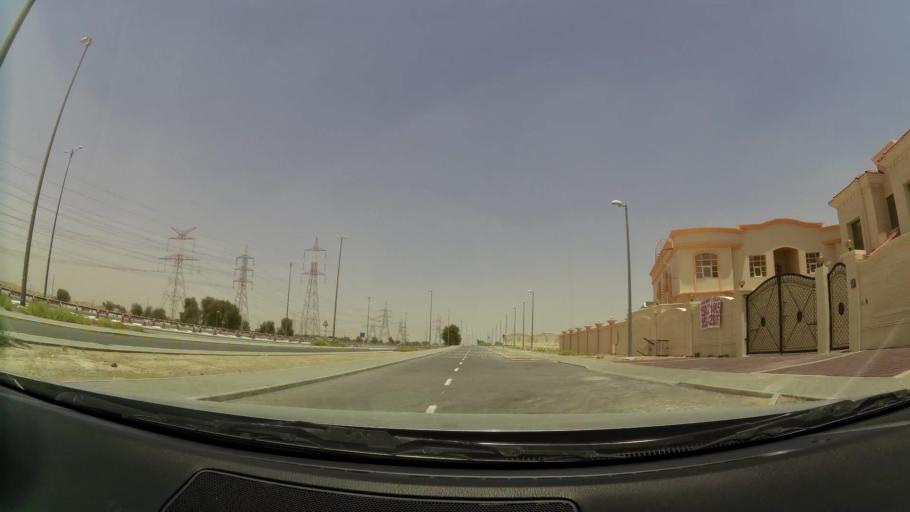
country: OM
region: Al Buraimi
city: Al Buraymi
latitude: 24.2727
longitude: 55.7130
